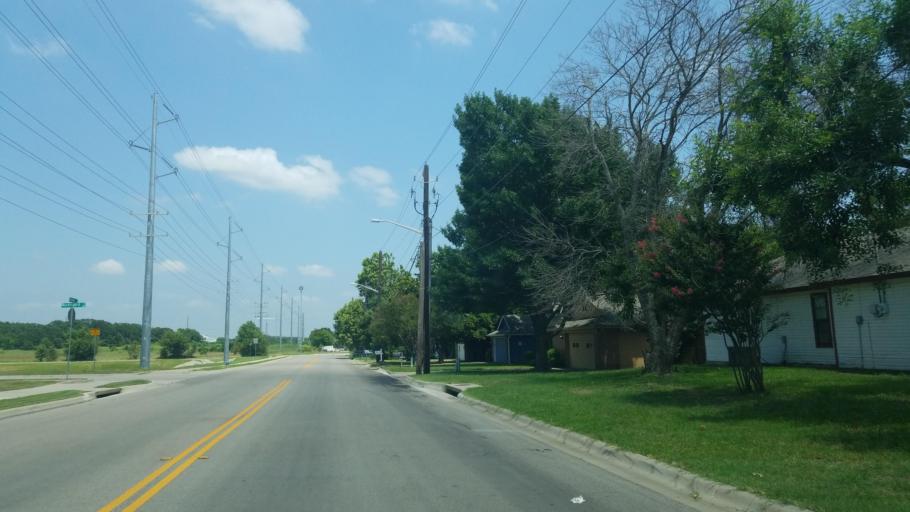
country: US
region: Texas
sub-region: Denton County
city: Denton
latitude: 33.2208
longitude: -97.0982
